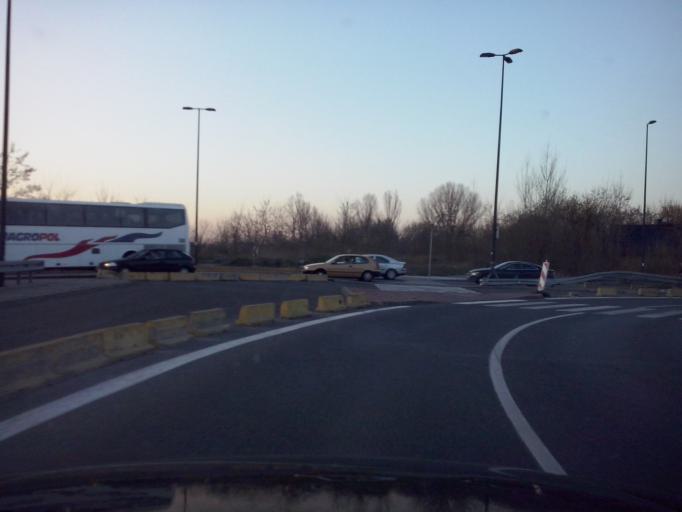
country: PL
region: Lesser Poland Voivodeship
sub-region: Krakow
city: Krakow
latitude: 50.0757
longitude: 19.9456
